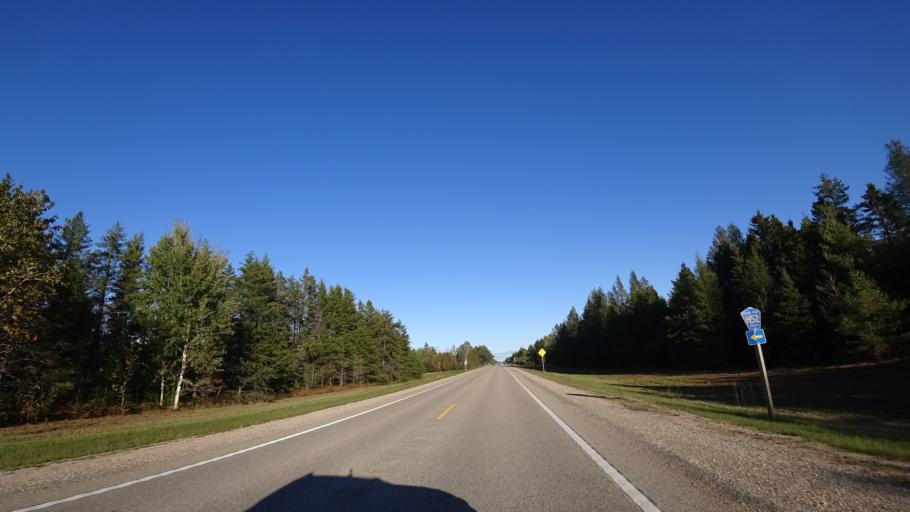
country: US
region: Michigan
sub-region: Alger County
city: Munising
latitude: 46.3462
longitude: -86.2806
